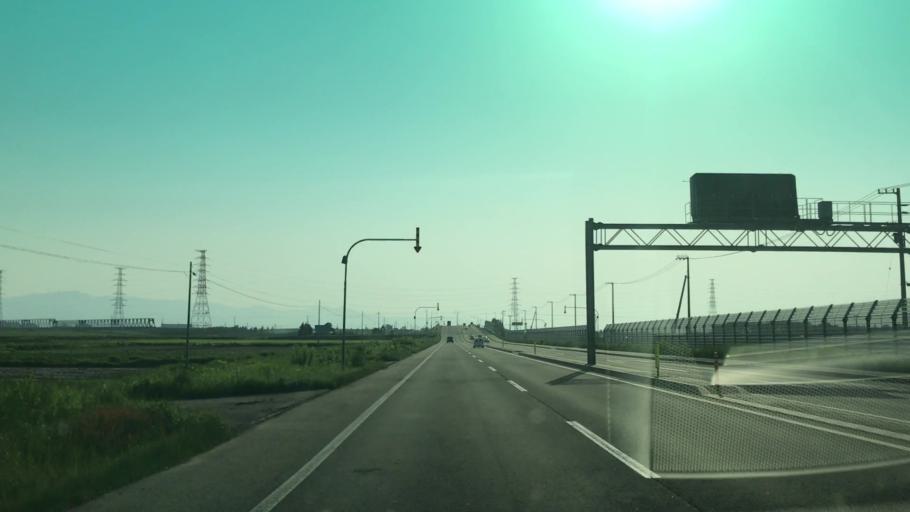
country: JP
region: Hokkaido
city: Tobetsu
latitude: 43.1774
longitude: 141.4409
